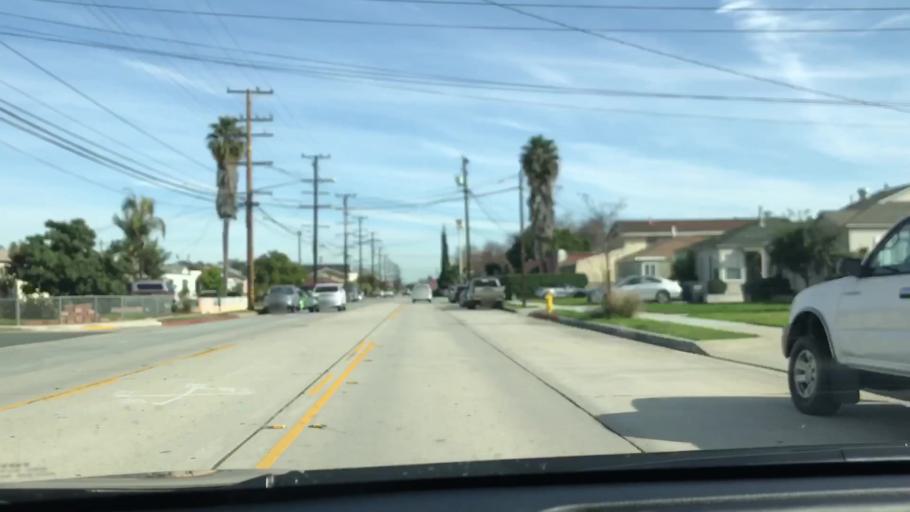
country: US
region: California
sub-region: Los Angeles County
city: Gardena
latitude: 33.8801
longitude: -118.3062
